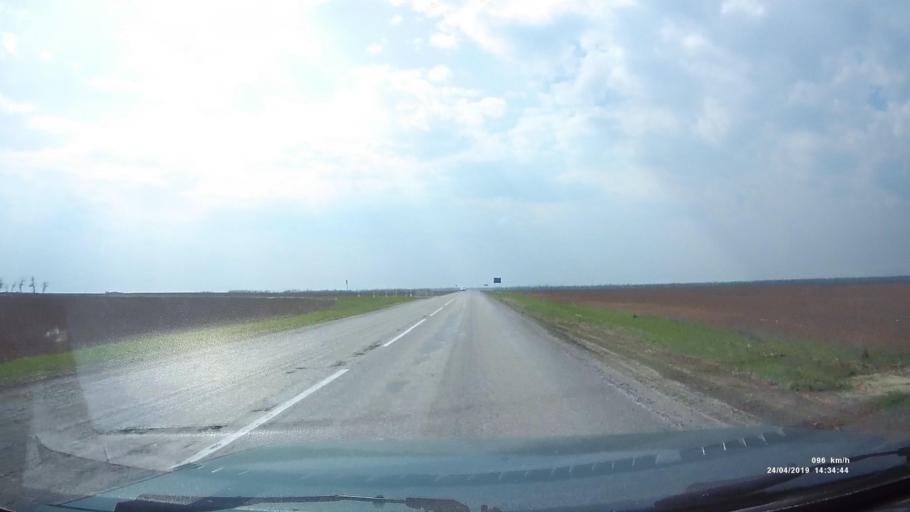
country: RU
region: Kalmykiya
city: Arshan'
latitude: 46.3738
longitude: 43.9264
